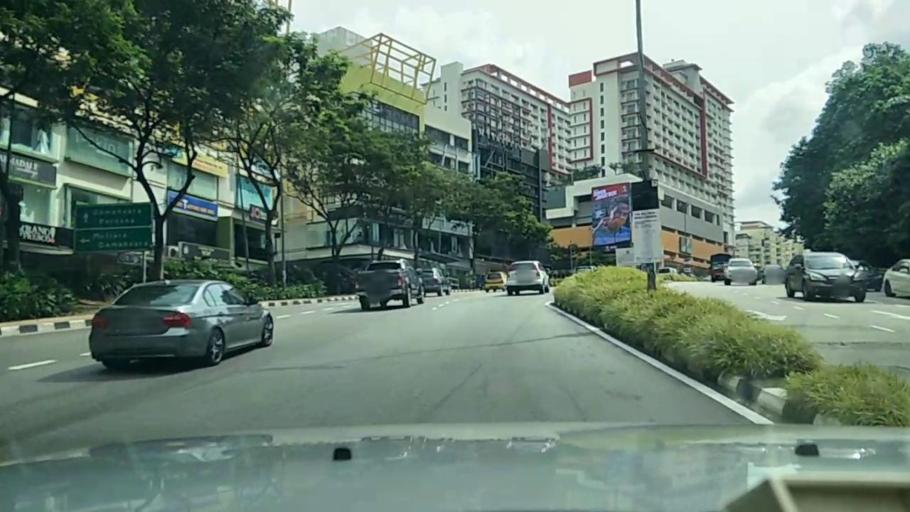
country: MY
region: Selangor
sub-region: Petaling
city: Petaling Jaya
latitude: 3.1650
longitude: 101.6129
